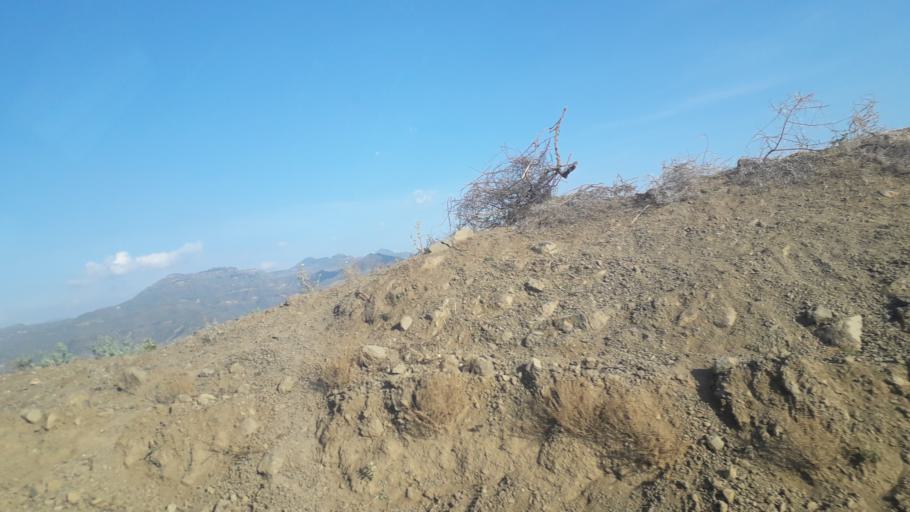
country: ET
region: Amhara
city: Dese
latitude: 11.5197
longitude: 39.2478
